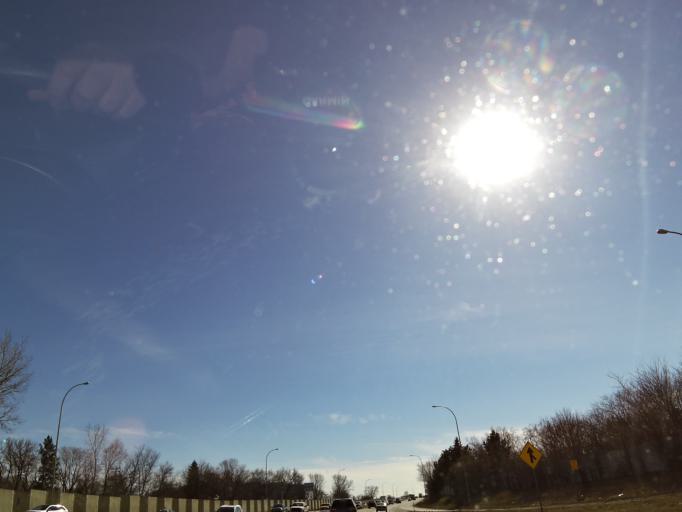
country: US
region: Minnesota
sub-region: Hennepin County
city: Minnetonka Mills
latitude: 44.9324
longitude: -93.3973
